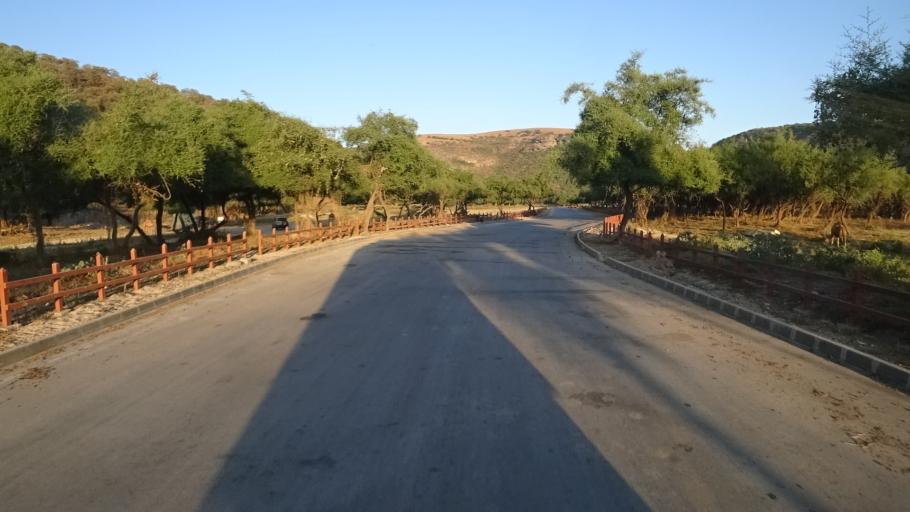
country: OM
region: Zufar
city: Salalah
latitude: 17.0908
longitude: 54.4392
